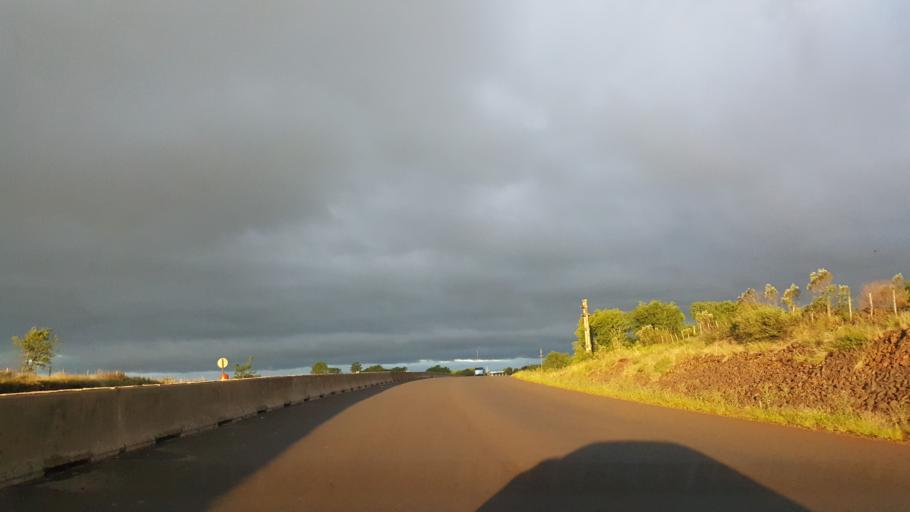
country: AR
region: Misiones
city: Cerro Cora
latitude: -27.4333
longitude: -55.6390
